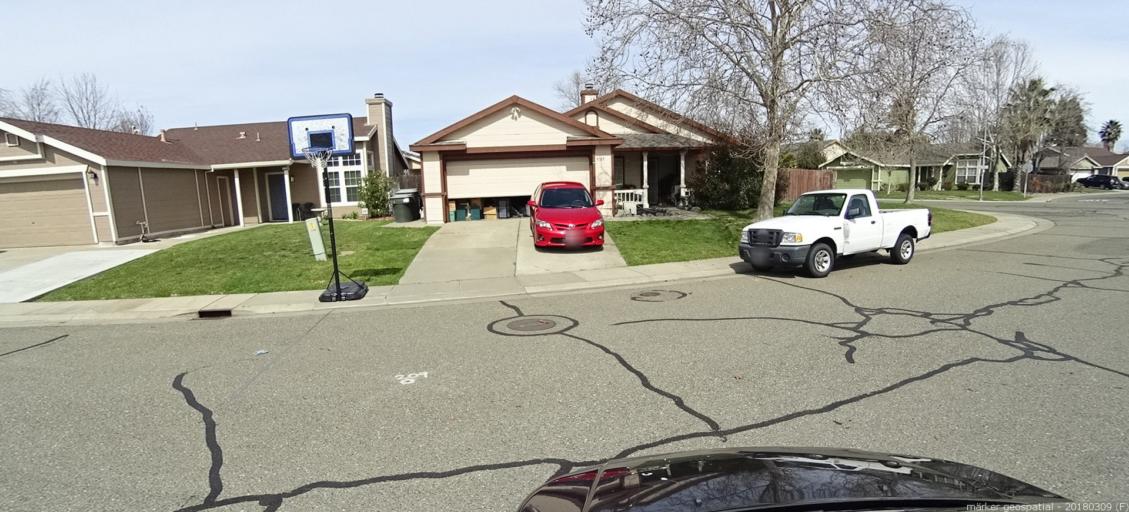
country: US
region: California
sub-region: Sacramento County
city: Vineyard
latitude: 38.4544
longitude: -121.3621
